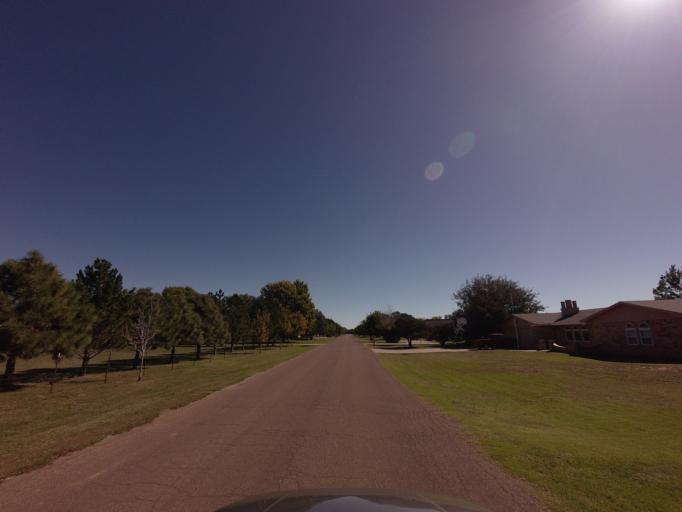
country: US
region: New Mexico
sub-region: Curry County
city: Clovis
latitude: 34.4275
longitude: -103.1764
